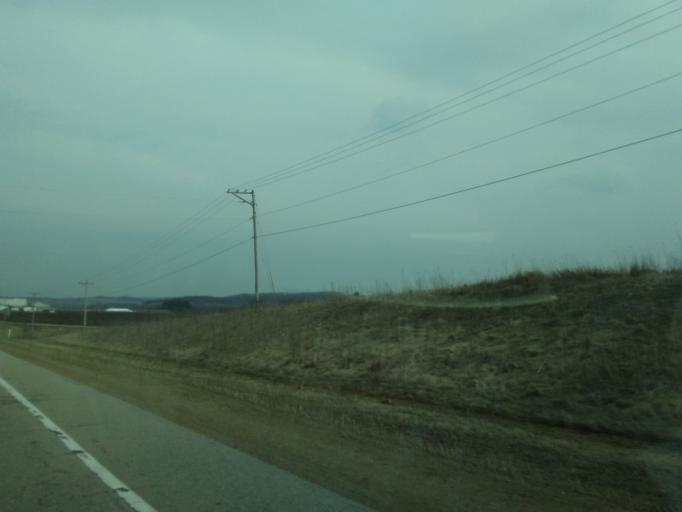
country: US
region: Wisconsin
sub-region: Columbia County
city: Lodi
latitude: 43.2629
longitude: -89.5211
